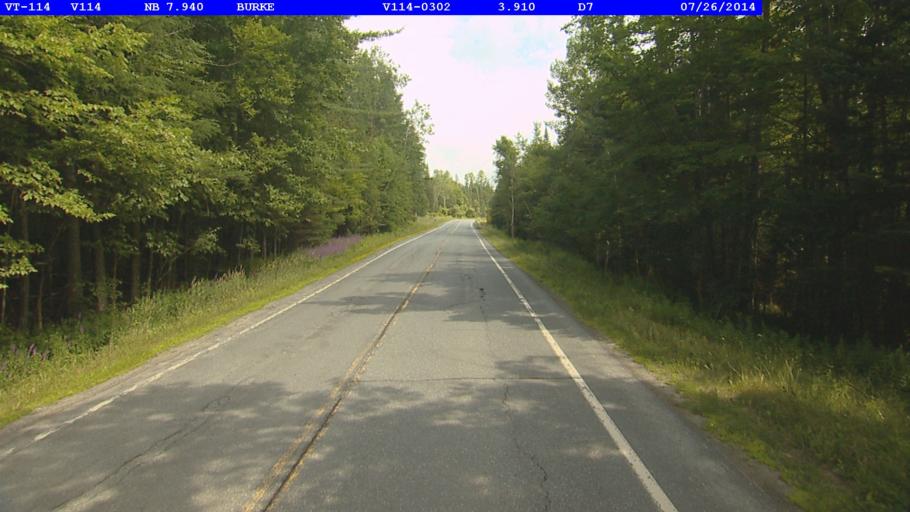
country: US
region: Vermont
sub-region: Caledonia County
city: Lyndonville
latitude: 44.6252
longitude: -71.9042
